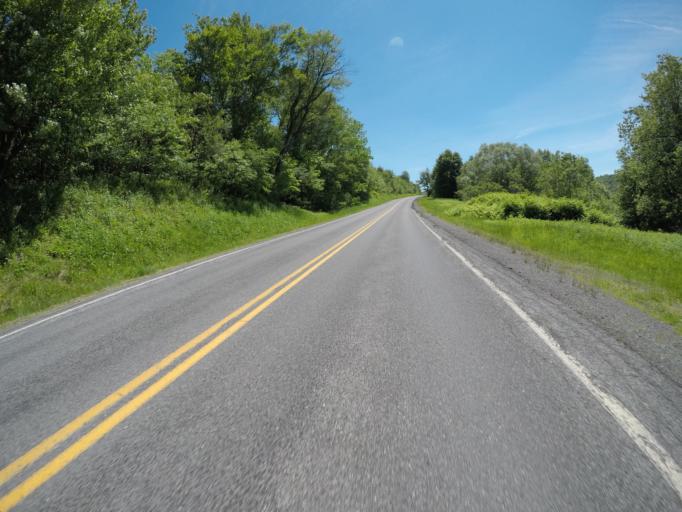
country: US
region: New York
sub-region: Delaware County
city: Delhi
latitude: 42.2111
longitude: -74.8693
